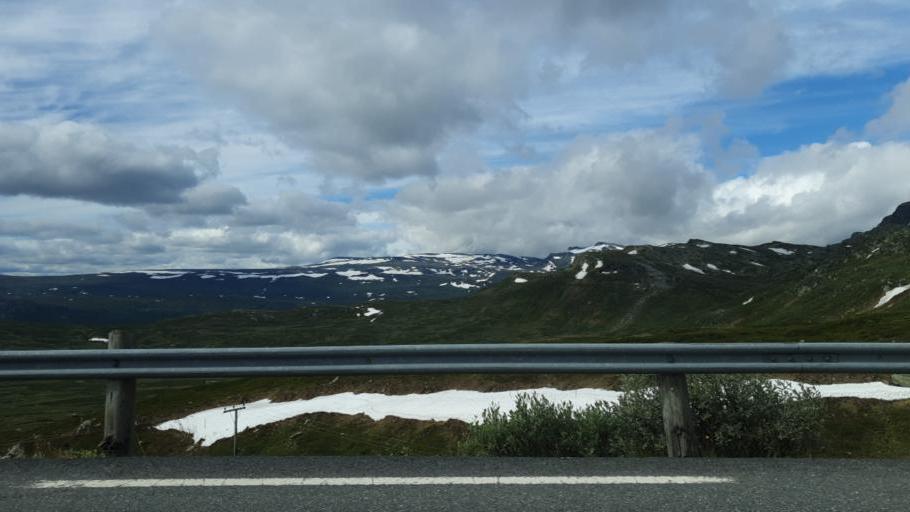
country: NO
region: Oppland
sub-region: Vestre Slidre
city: Slidre
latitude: 61.2874
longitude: 8.8141
